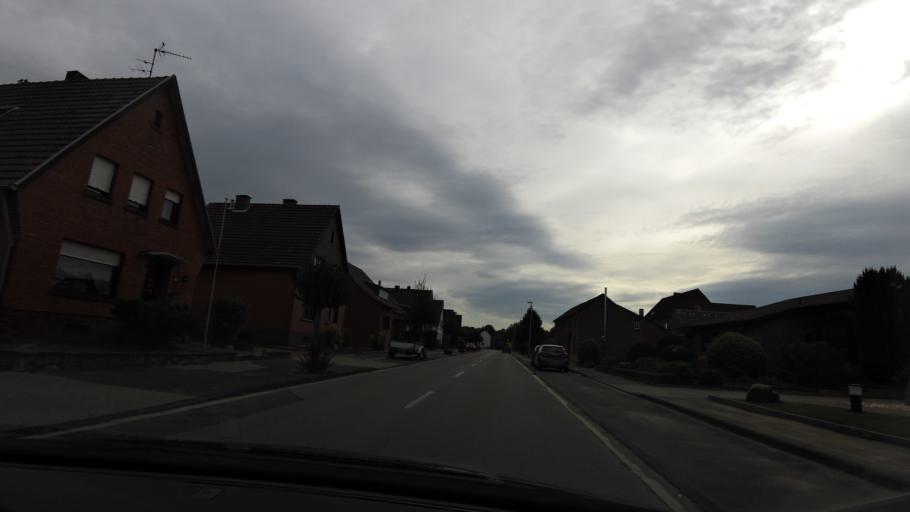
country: DE
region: North Rhine-Westphalia
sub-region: Regierungsbezirk Koln
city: Gangelt
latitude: 50.9798
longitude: 6.0342
